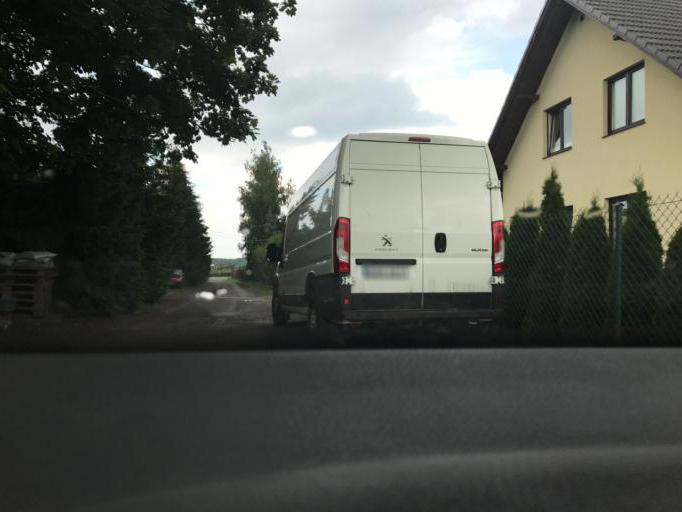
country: PL
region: Pomeranian Voivodeship
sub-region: Powiat gdanski
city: Cedry Wielkie
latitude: 54.3387
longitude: 18.8171
